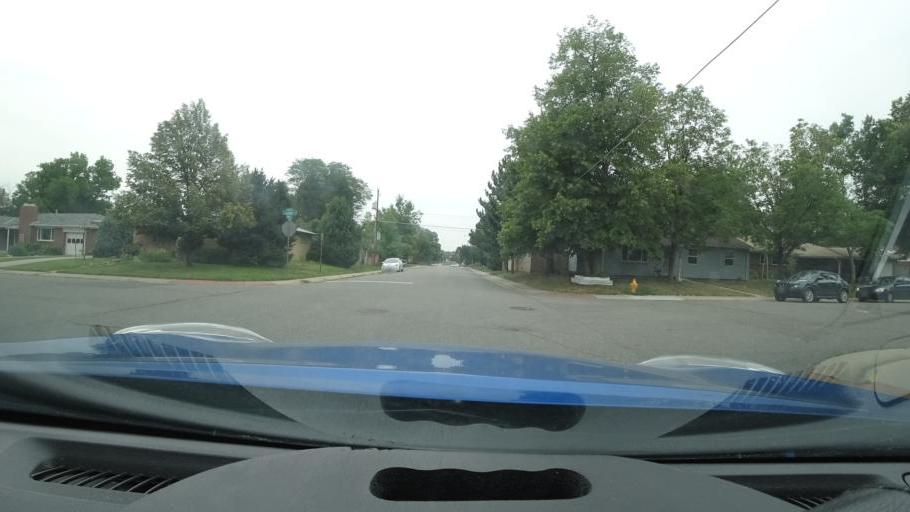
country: US
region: Colorado
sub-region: Arapahoe County
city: Glendale
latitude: 39.6858
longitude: -104.9152
